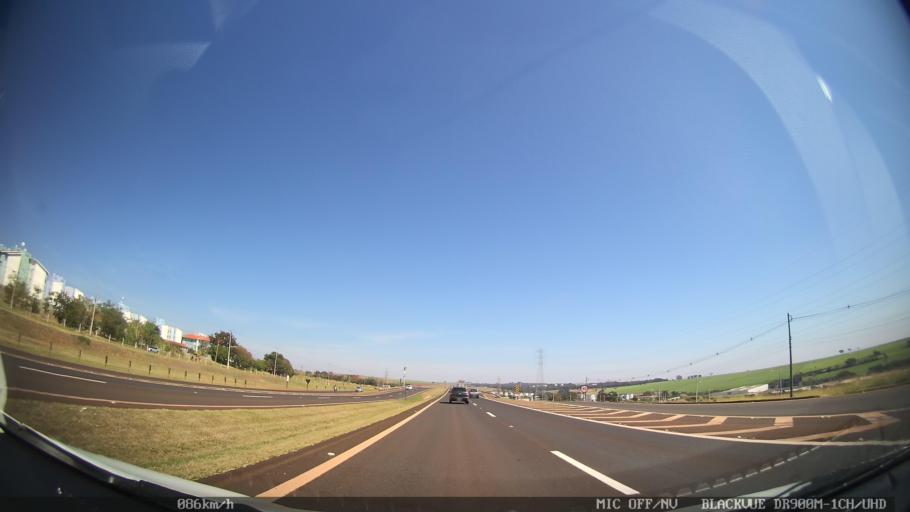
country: BR
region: Sao Paulo
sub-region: Ribeirao Preto
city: Ribeirao Preto
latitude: -21.1323
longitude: -47.8540
